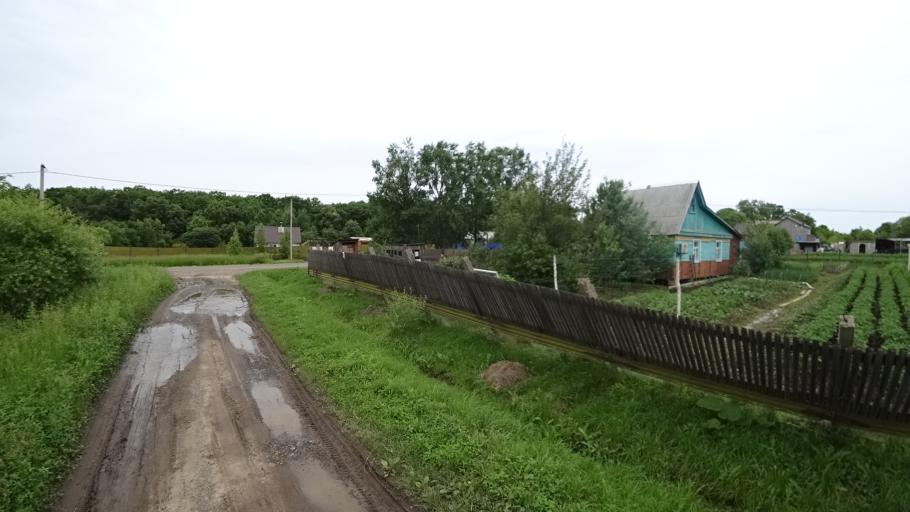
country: RU
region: Primorskiy
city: Novosysoyevka
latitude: 44.2087
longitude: 133.3345
